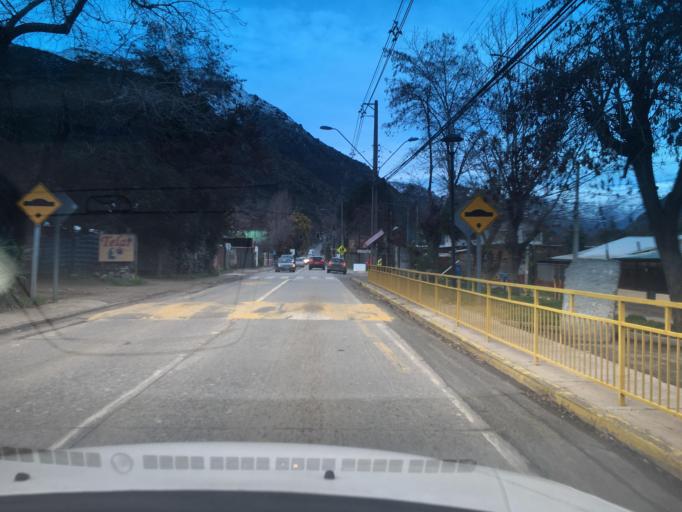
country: CL
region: Santiago Metropolitan
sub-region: Provincia de Cordillera
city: Puente Alto
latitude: -33.5763
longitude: -70.4512
